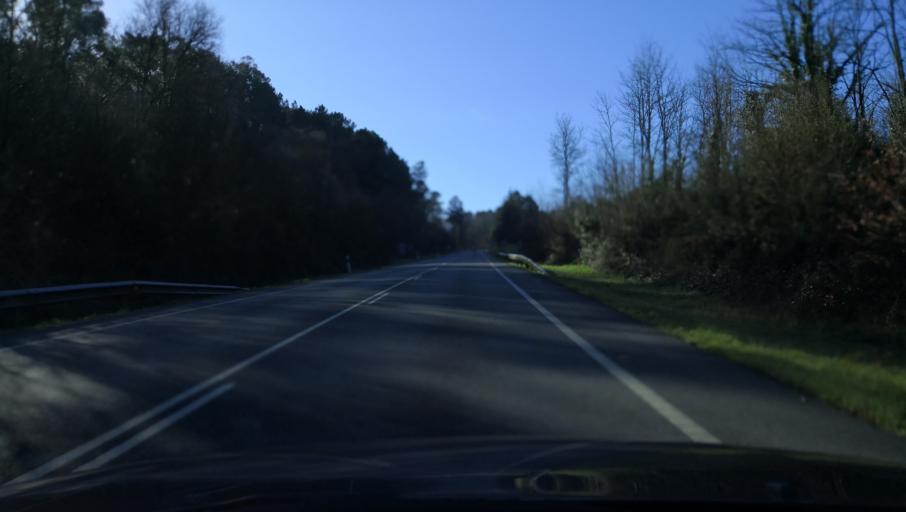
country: ES
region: Galicia
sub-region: Provincia da Coruna
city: Ribeira
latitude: 42.7700
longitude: -8.3981
